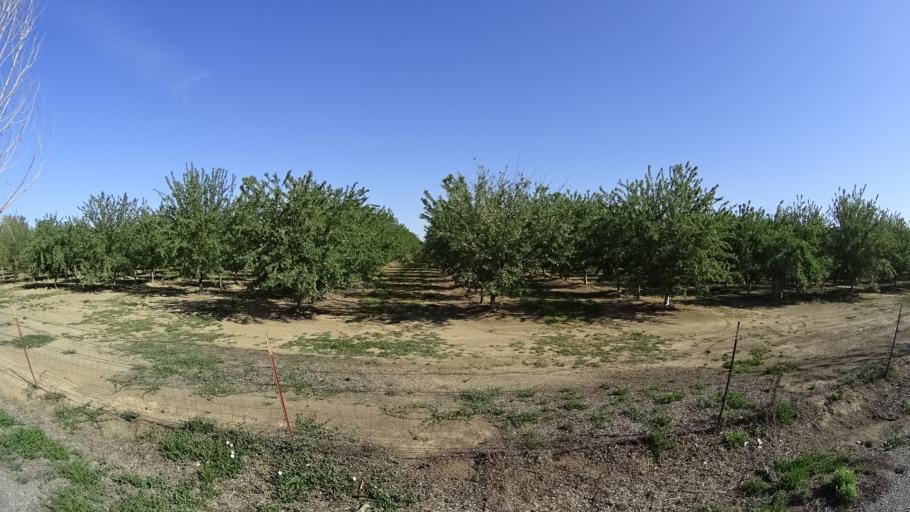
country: US
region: California
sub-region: Glenn County
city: Orland
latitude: 39.6826
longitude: -122.2109
